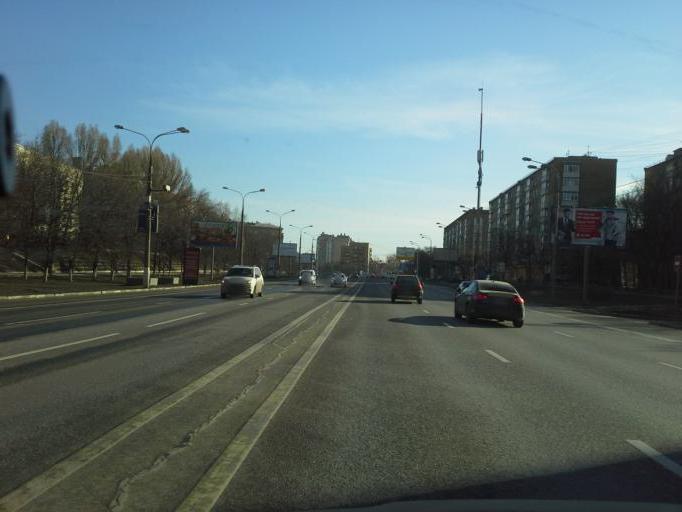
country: RU
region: Moscow
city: Taganskiy
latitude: 55.7212
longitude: 37.6636
